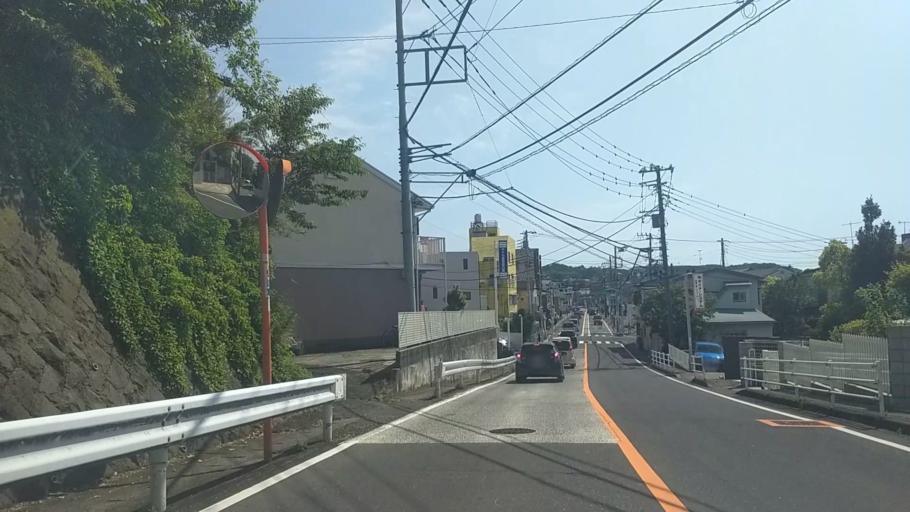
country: JP
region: Kanagawa
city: Kamakura
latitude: 35.3472
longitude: 139.5422
